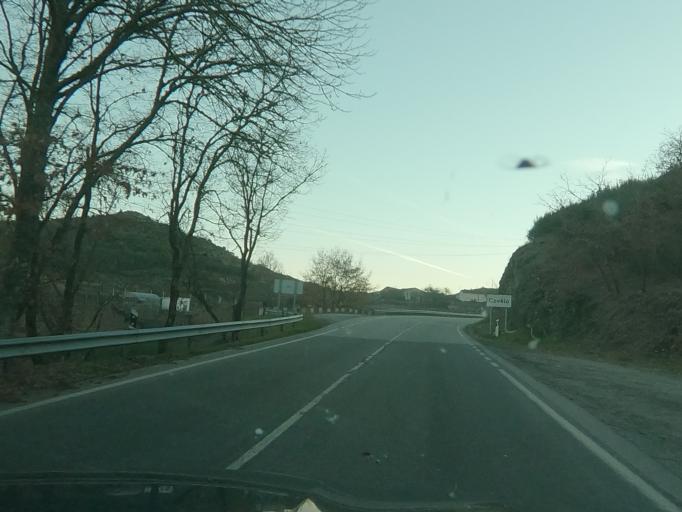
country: PT
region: Vila Real
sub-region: Vila Pouca de Aguiar
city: Vila Pouca de Aguiar
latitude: 41.4130
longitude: -7.6873
